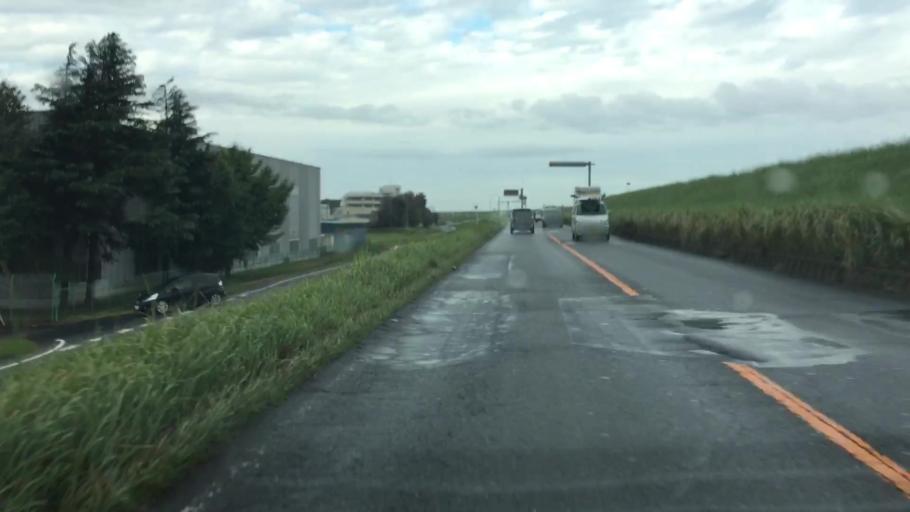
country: JP
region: Ibaraki
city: Toride
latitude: 35.8789
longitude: 140.0954
